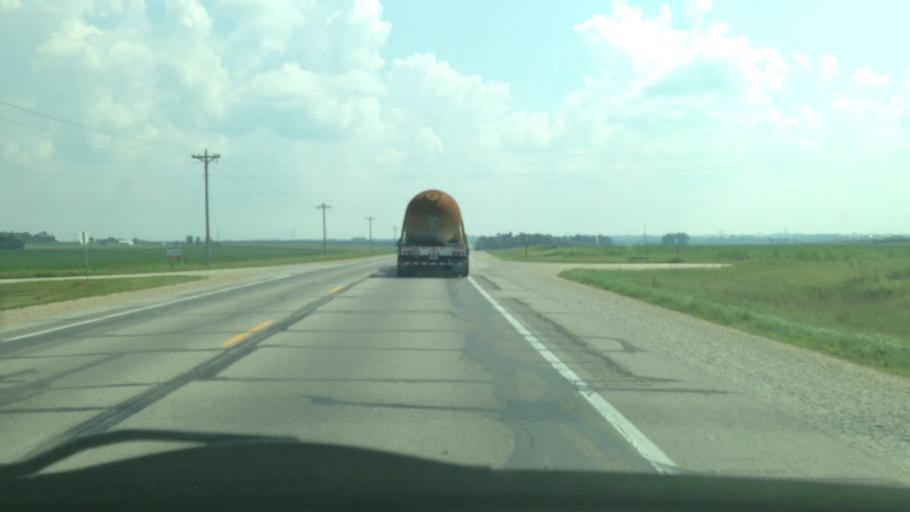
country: US
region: Iowa
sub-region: Chickasaw County
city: New Hampton
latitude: 43.1272
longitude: -92.2980
